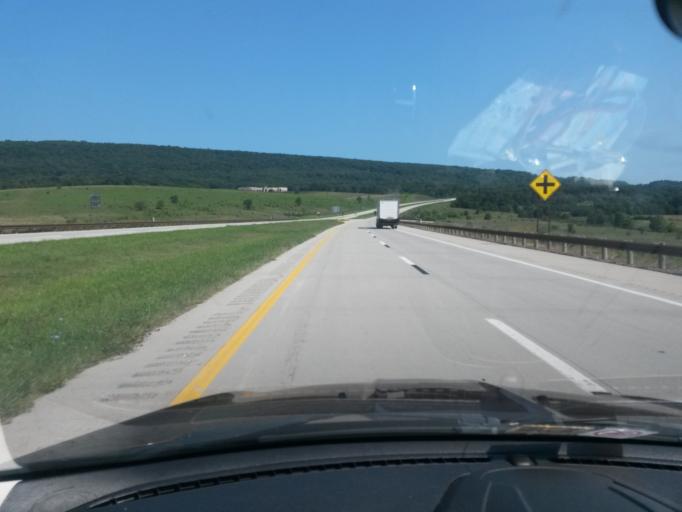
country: US
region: West Virginia
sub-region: Hardy County
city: Moorefield
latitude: 39.0930
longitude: -78.9844
